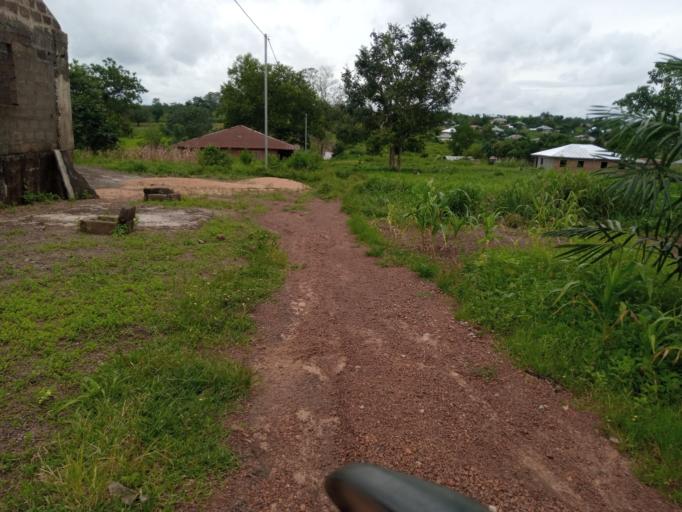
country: SL
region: Southern Province
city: Largo
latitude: 8.2006
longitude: -12.0566
